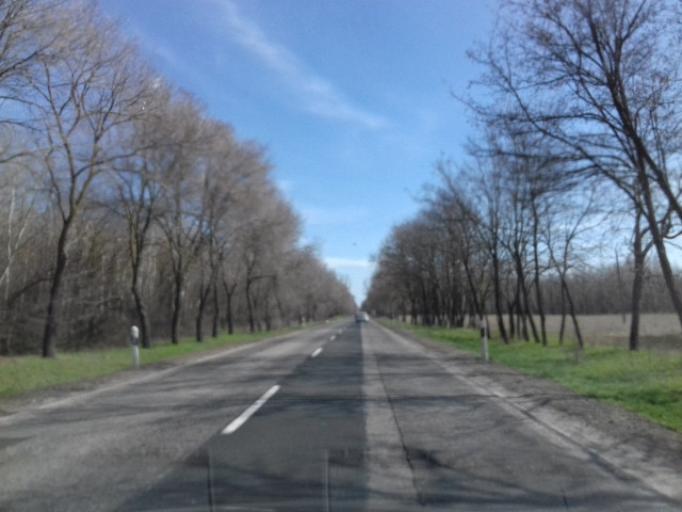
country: HU
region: Bacs-Kiskun
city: Nyarlorinc
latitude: 46.9034
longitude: 19.8153
